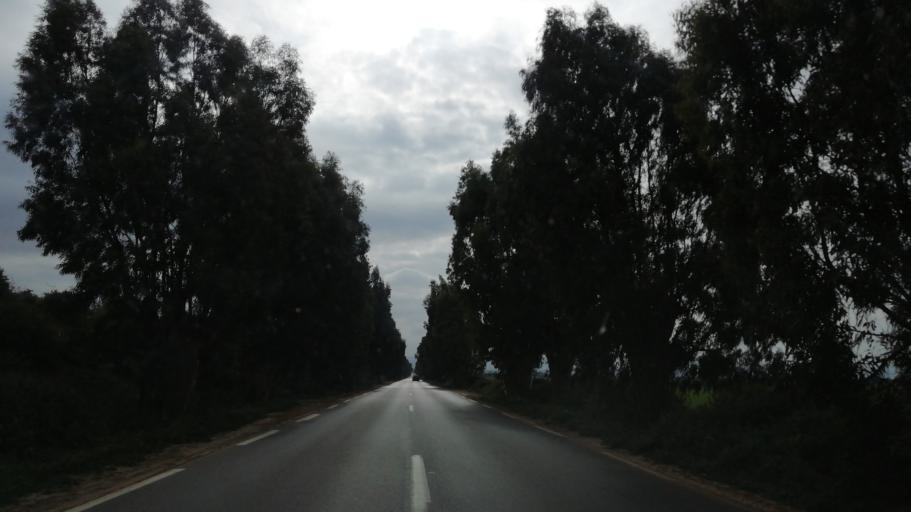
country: DZ
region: Oran
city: Sidi ech Chahmi
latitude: 35.5829
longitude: -0.4527
